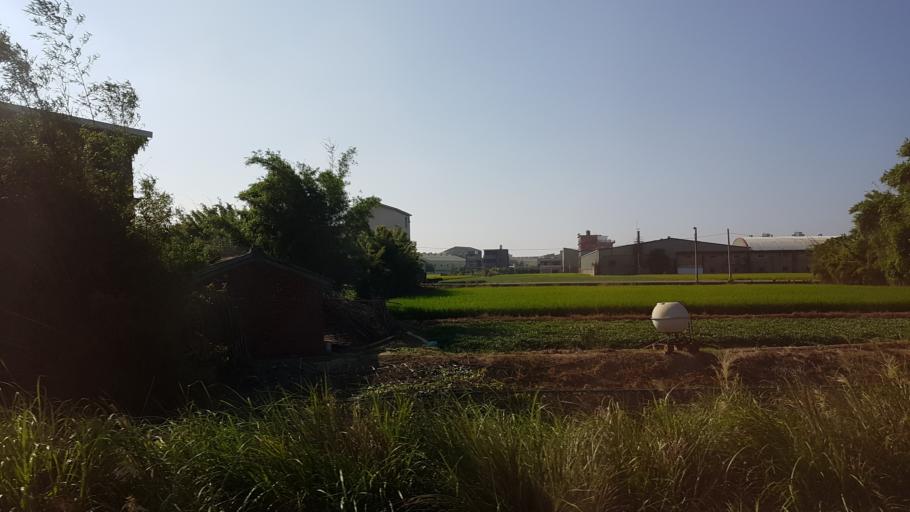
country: TW
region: Taiwan
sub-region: Miaoli
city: Miaoli
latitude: 24.6545
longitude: 120.8763
